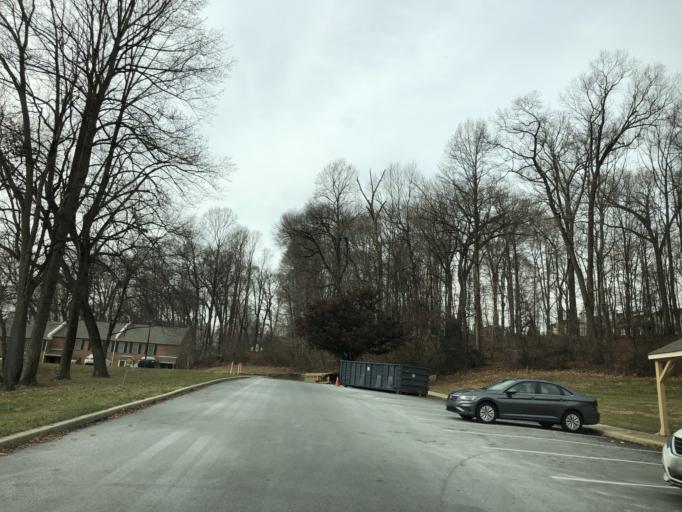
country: US
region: Pennsylvania
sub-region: Chester County
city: Exton
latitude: 40.0325
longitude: -75.6389
